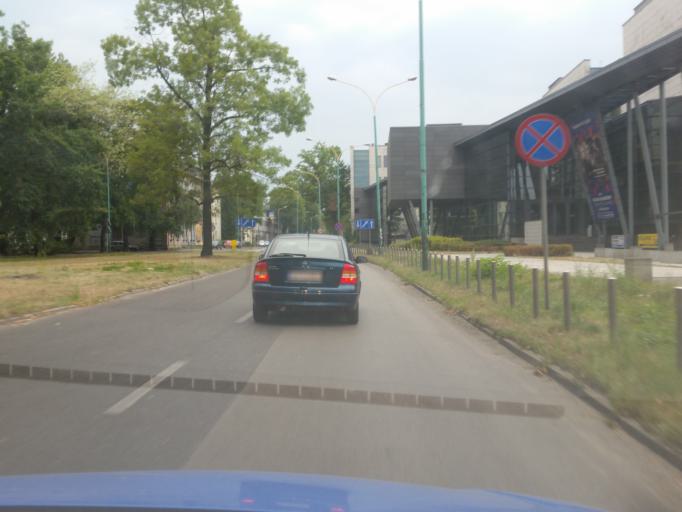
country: PL
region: Silesian Voivodeship
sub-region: Sosnowiec
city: Sosnowiec
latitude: 50.2854
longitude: 19.1312
